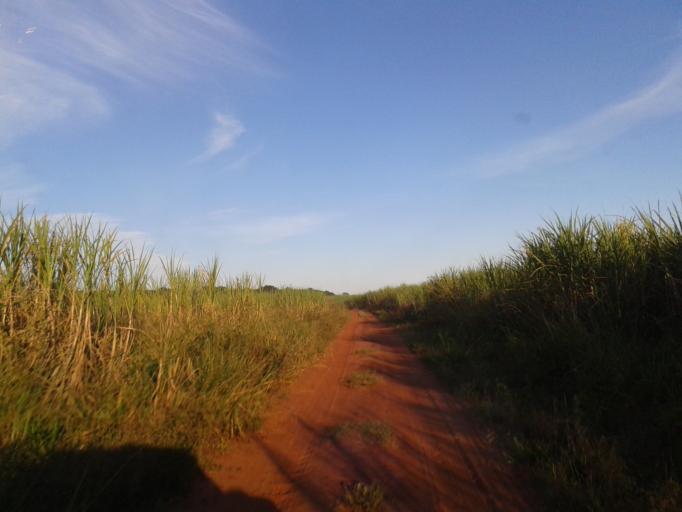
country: BR
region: Minas Gerais
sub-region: Santa Vitoria
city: Santa Vitoria
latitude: -19.0045
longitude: -50.3833
